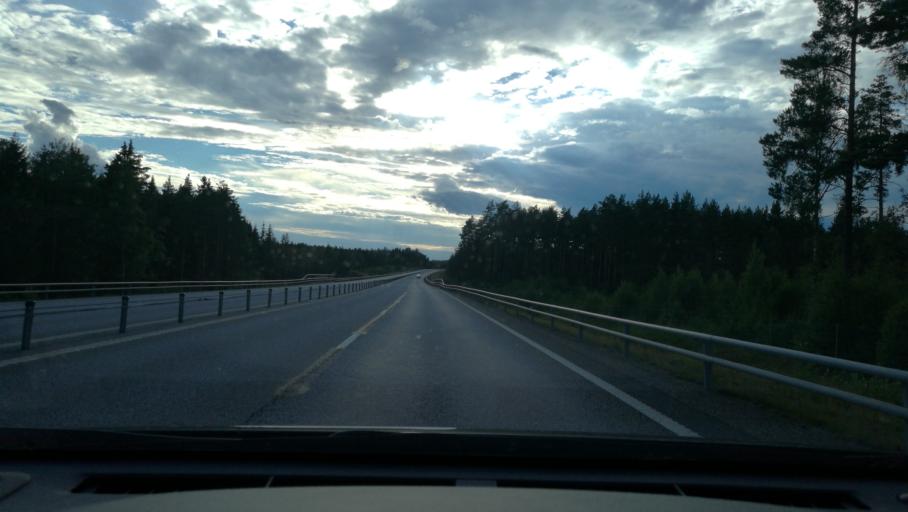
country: SE
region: OEstergoetland
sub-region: Norrkopings Kommun
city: Svartinge
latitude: 58.6672
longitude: 16.0097
